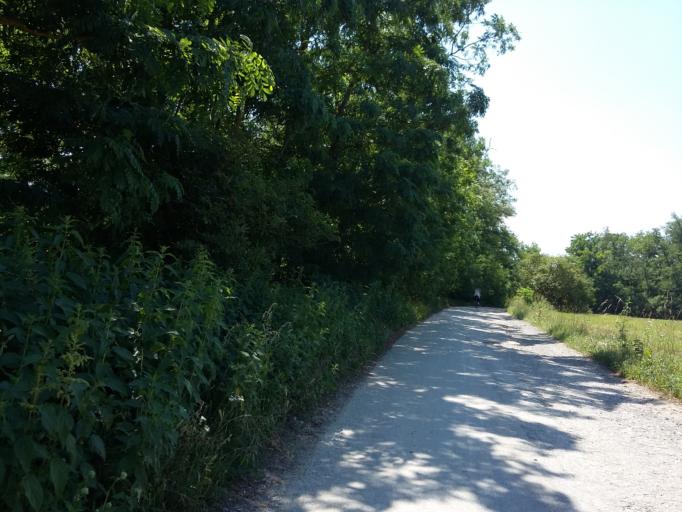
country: AT
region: Lower Austria
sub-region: Politischer Bezirk Ganserndorf
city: Marchegg
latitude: 48.2770
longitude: 16.9662
